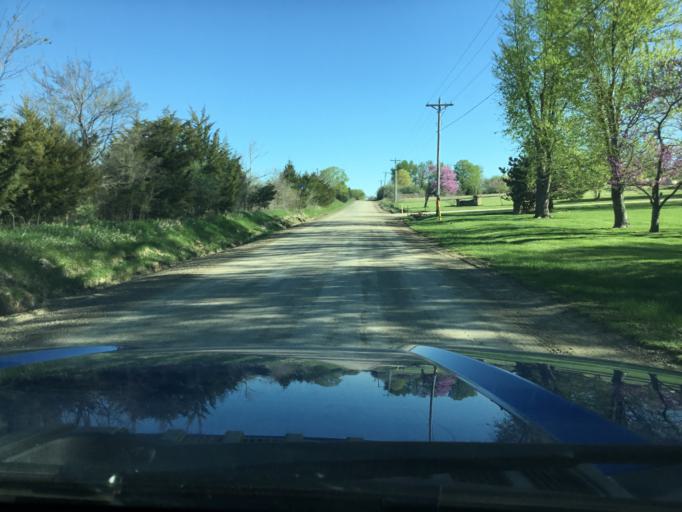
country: US
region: Kansas
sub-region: Douglas County
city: Lawrence
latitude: 38.9866
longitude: -95.3539
